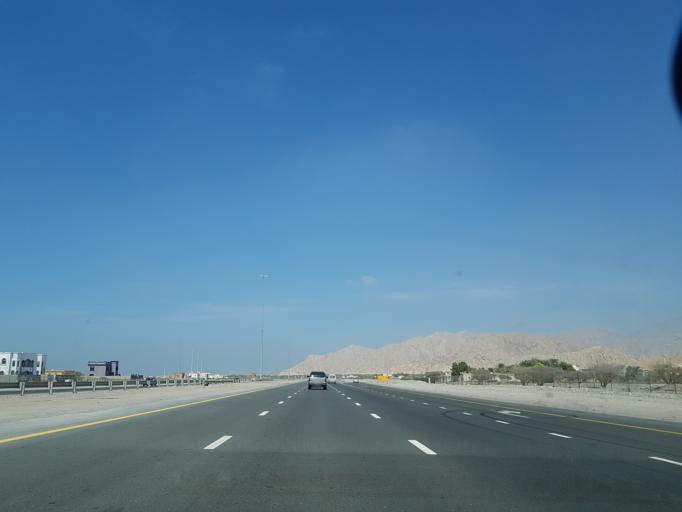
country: AE
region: Ra's al Khaymah
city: Ras al-Khaimah
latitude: 25.7930
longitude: 56.0312
